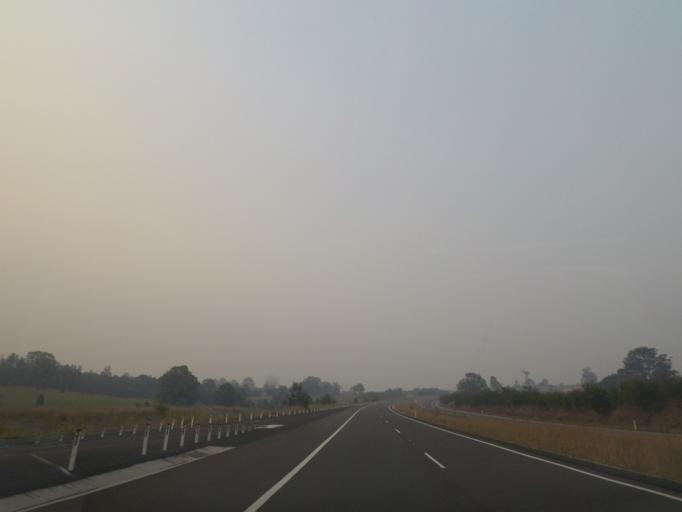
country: AU
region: New South Wales
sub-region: Nambucca Shire
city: Macksville
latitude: -30.7624
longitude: 152.9041
